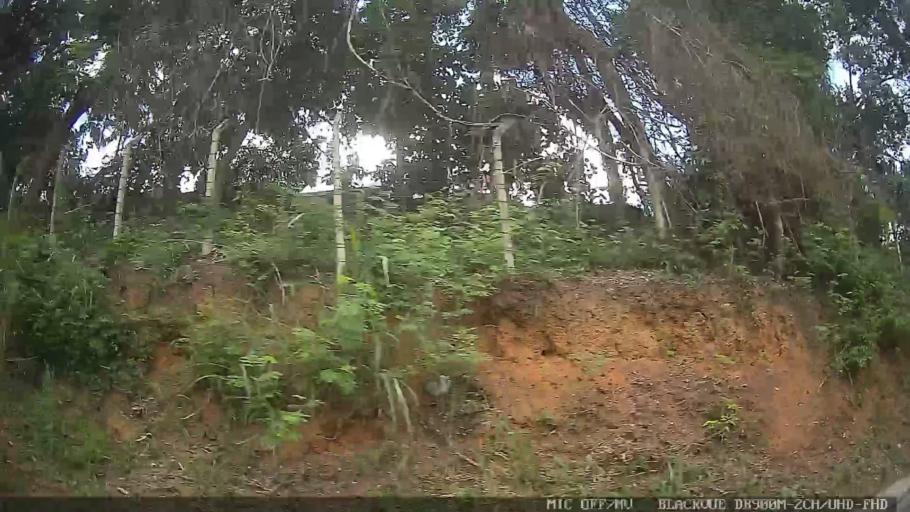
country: BR
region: Sao Paulo
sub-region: Jarinu
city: Jarinu
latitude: -23.0768
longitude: -46.6422
